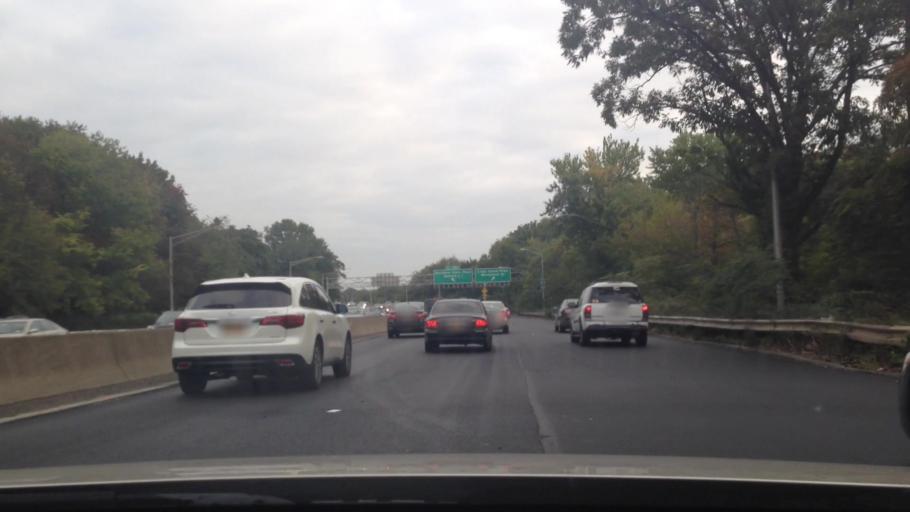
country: US
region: New York
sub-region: Nassau County
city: Elmont
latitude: 40.6821
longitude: -73.7274
